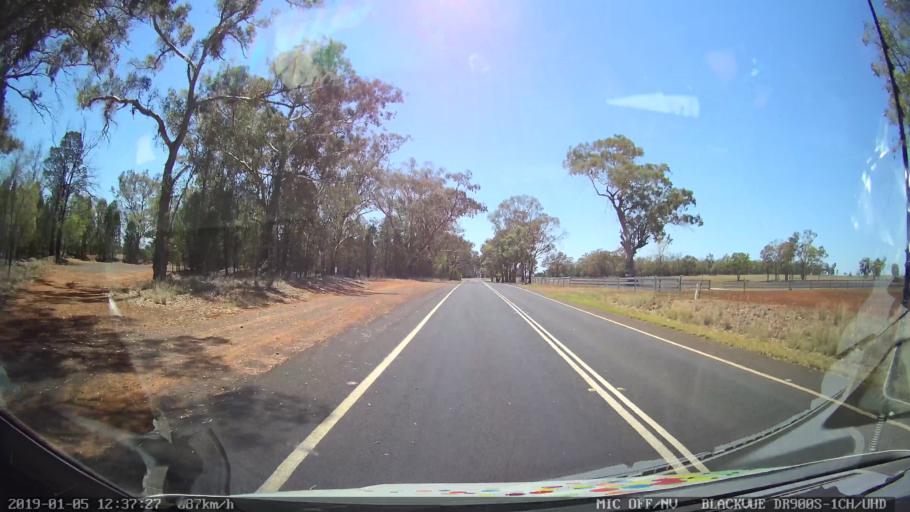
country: AU
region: New South Wales
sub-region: Warrumbungle Shire
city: Coonabarabran
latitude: -31.2032
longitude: 149.4549
